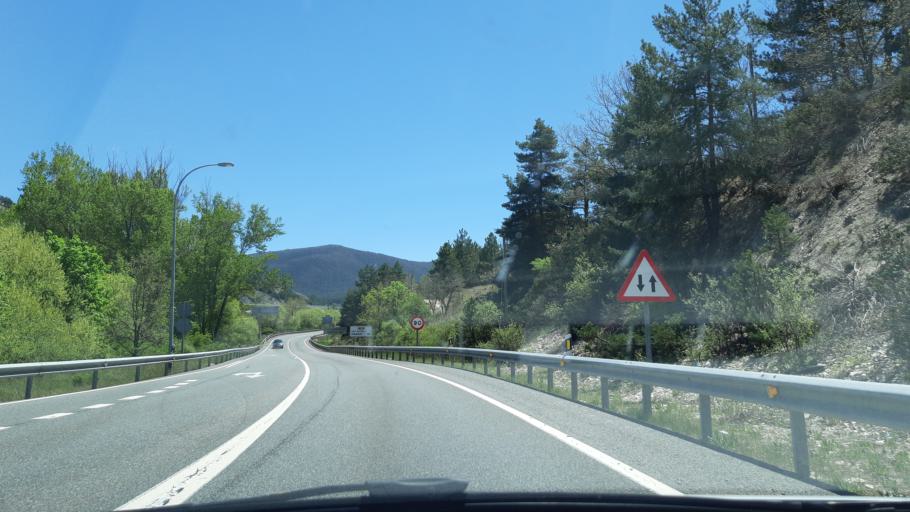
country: ES
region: Castille and Leon
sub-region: Provincia de Segovia
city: Otero de Herreros
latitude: 40.7257
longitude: -4.1959
